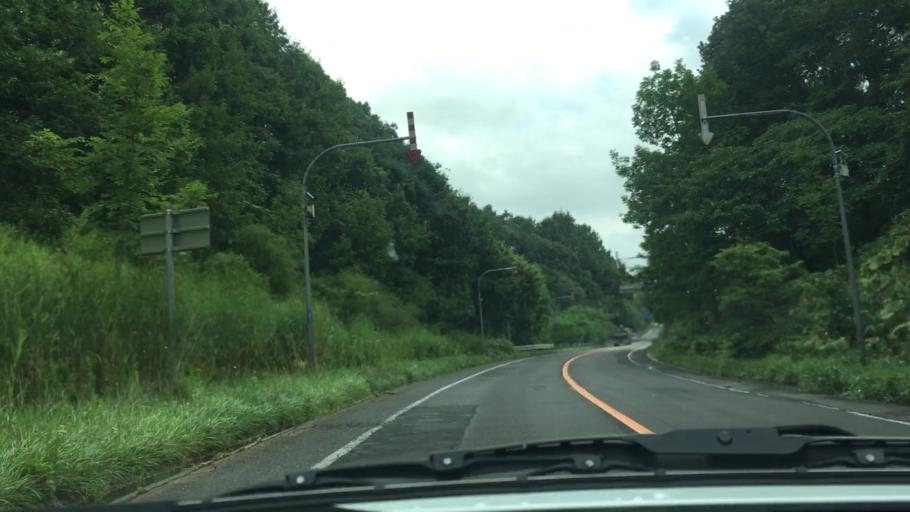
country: JP
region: Hokkaido
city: Chitose
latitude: 42.9454
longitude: 141.7394
